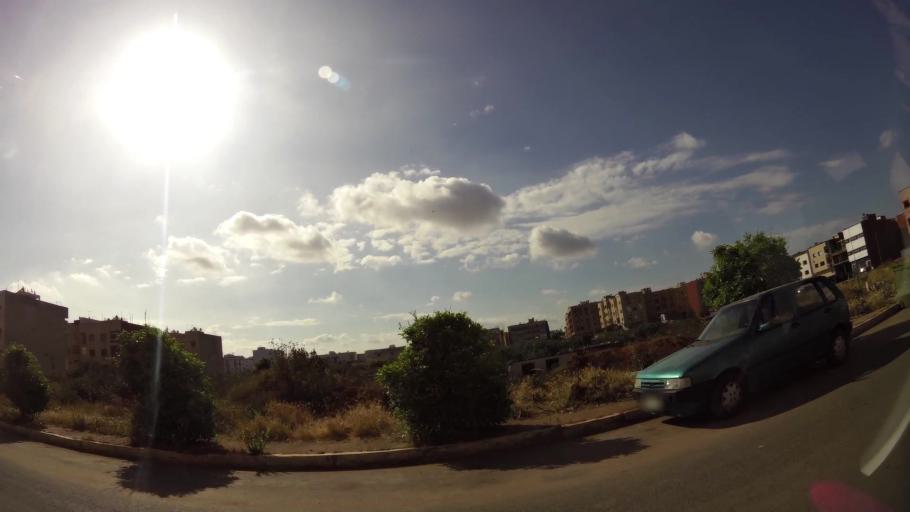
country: MA
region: Rabat-Sale-Zemmour-Zaer
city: Sale
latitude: 34.0604
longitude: -6.8080
